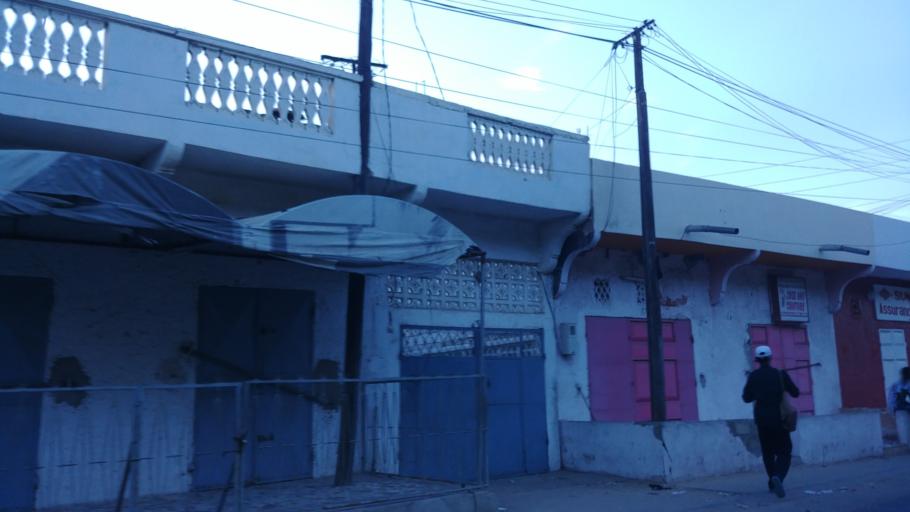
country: SN
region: Saint-Louis
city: Saint-Louis
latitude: 16.0162
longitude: -16.4901
